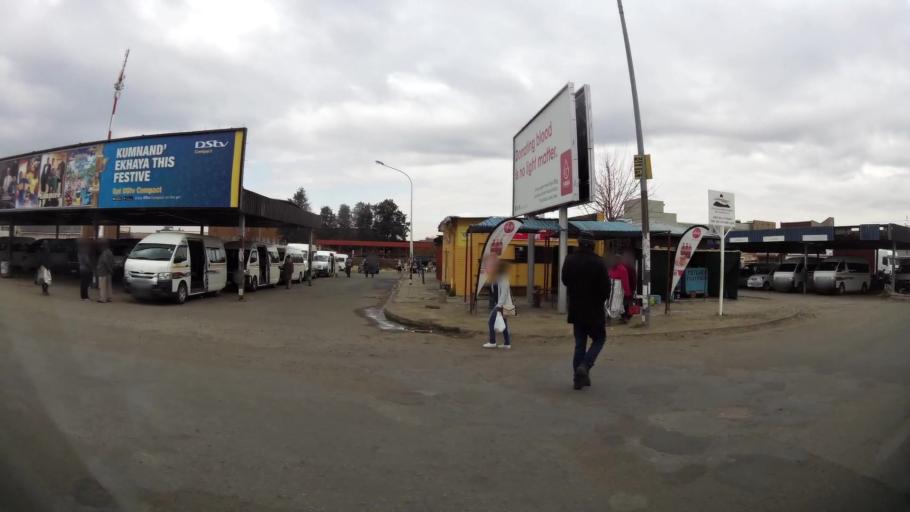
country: ZA
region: Orange Free State
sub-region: Fezile Dabi District Municipality
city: Kroonstad
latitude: -27.6606
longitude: 27.2338
